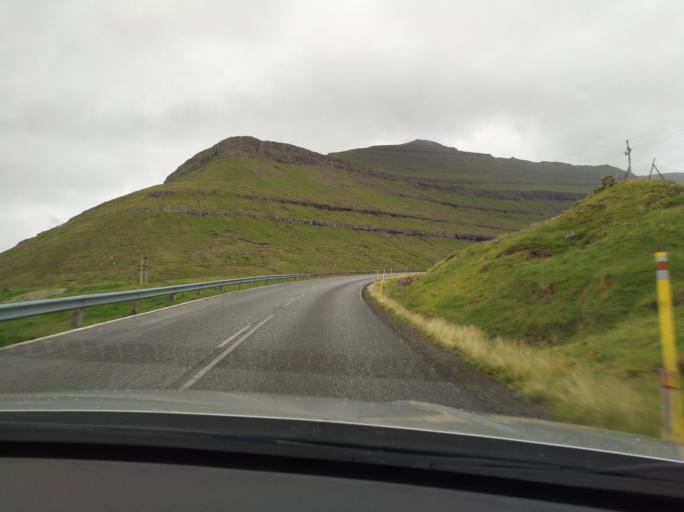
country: FO
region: Eysturoy
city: Fuglafjordur
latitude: 62.2231
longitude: -6.8783
